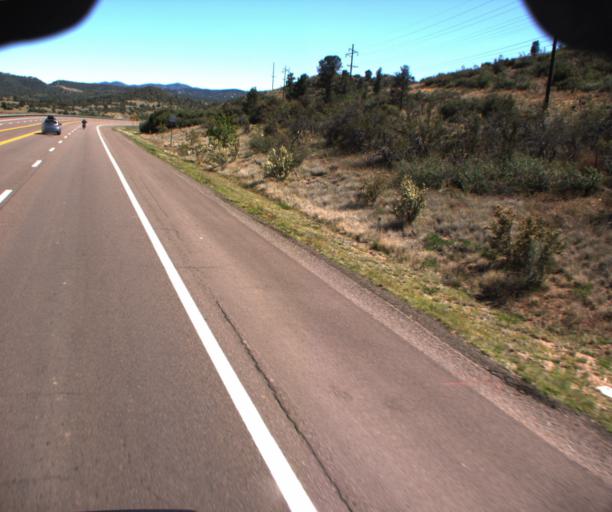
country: US
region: Arizona
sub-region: Yavapai County
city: Prescott
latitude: 34.5892
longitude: -112.4248
